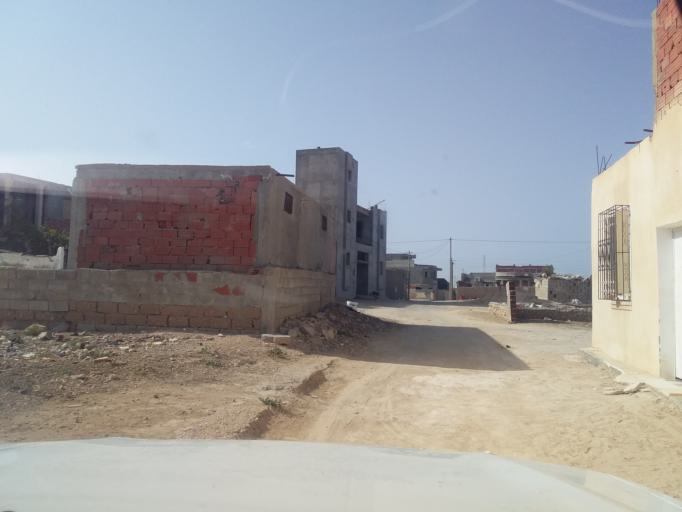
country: TN
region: Qabis
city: Gabes
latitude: 33.6409
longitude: 10.2965
